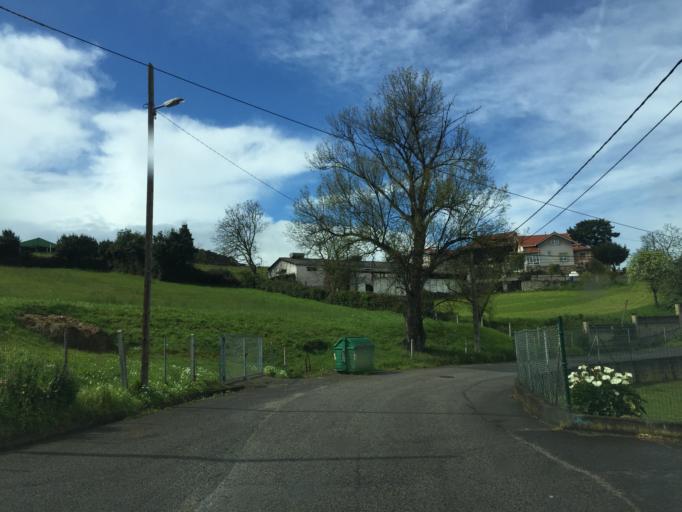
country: ES
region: Asturias
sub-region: Province of Asturias
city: Natahoyo
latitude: 43.5537
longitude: -5.7078
